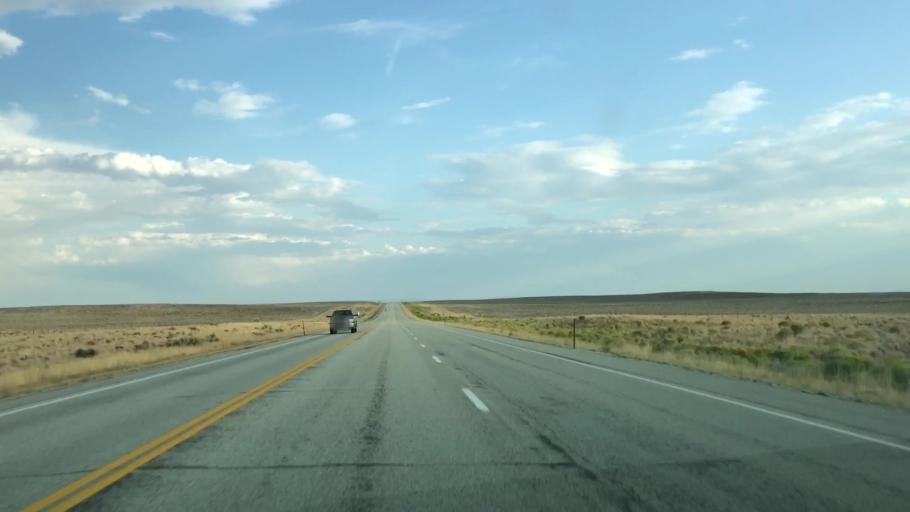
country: US
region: Wyoming
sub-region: Sweetwater County
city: North Rock Springs
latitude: 42.2728
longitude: -109.4804
